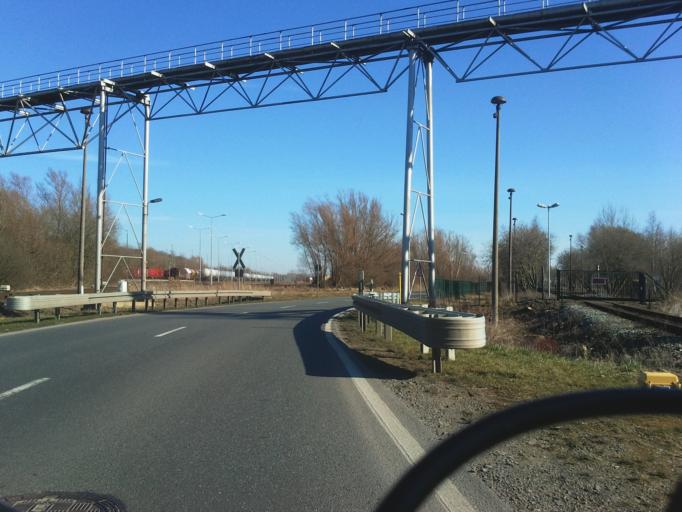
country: DE
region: Mecklenburg-Vorpommern
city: Nienhagen
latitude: 54.1464
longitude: 12.1483
